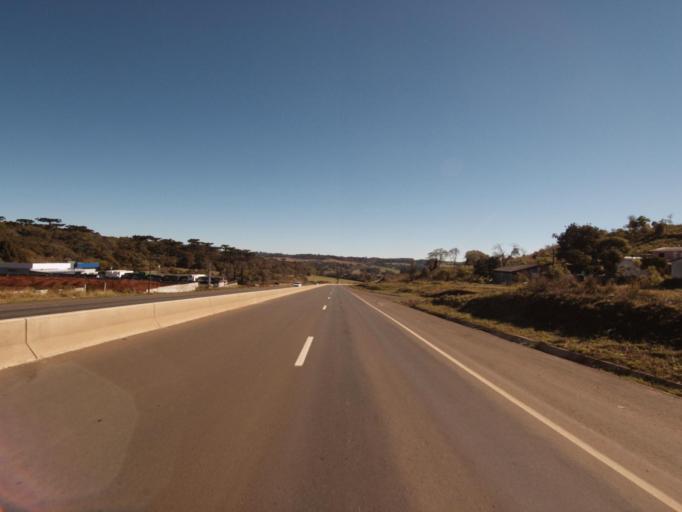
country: BR
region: Santa Catarina
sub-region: Xanxere
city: Xanxere
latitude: -26.8860
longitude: -52.4214
